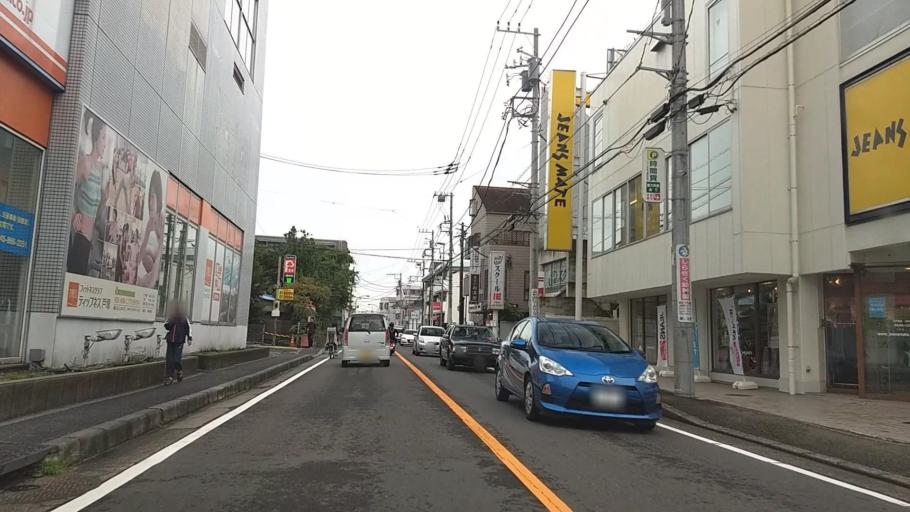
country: JP
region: Kanagawa
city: Fujisawa
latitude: 35.3978
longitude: 139.5362
